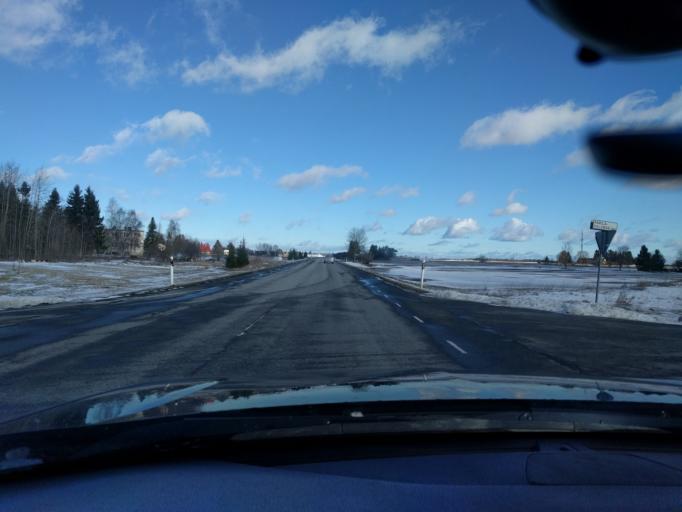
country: EE
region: Harju
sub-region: Raasiku vald
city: Raasiku
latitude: 59.3659
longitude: 25.1895
